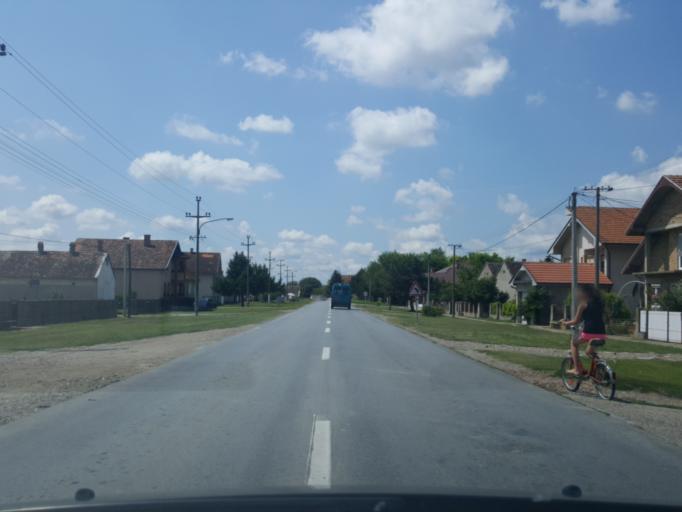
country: RS
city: Salas Nocajski
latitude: 44.9449
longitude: 19.5816
